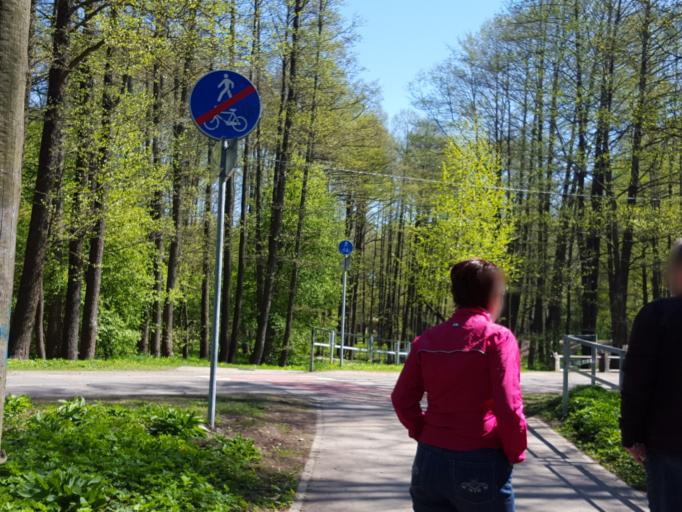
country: LV
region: Marupe
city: Marupe
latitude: 56.9173
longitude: 24.0517
